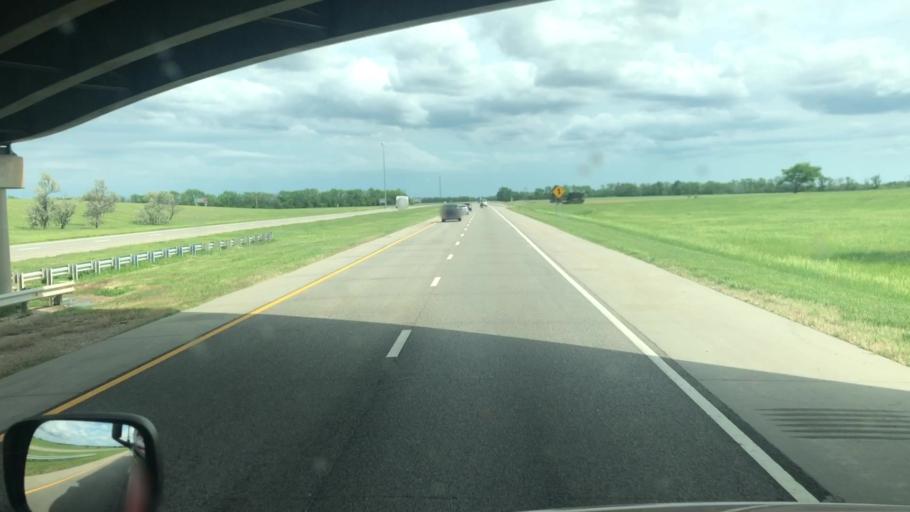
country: US
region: Kansas
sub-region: McPherson County
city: Moundridge
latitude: 38.2029
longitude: -97.4874
